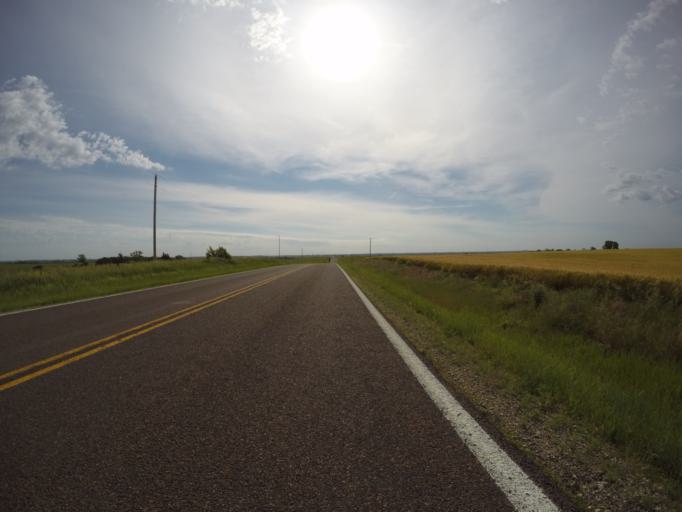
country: US
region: Kansas
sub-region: Washington County
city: Washington
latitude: 39.7124
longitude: -97.2950
